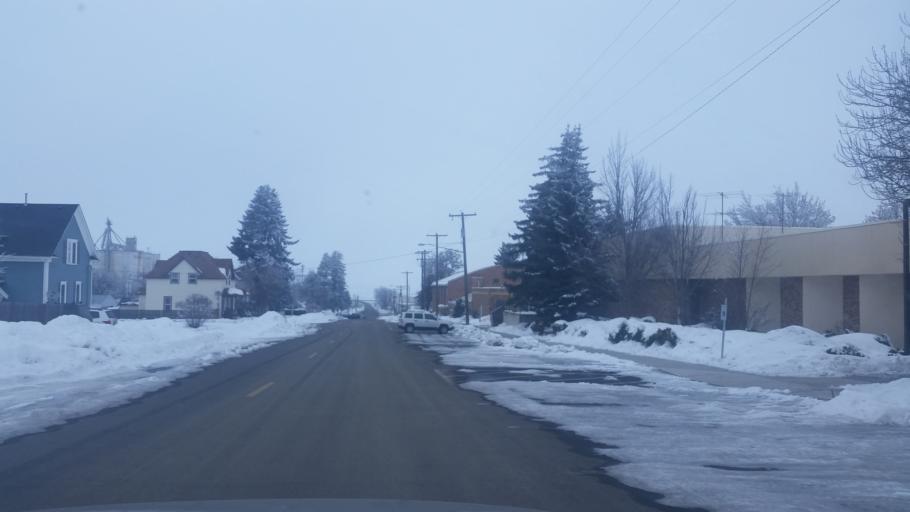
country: US
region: Washington
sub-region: Spokane County
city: Medical Lake
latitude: 47.6666
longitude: -117.8779
